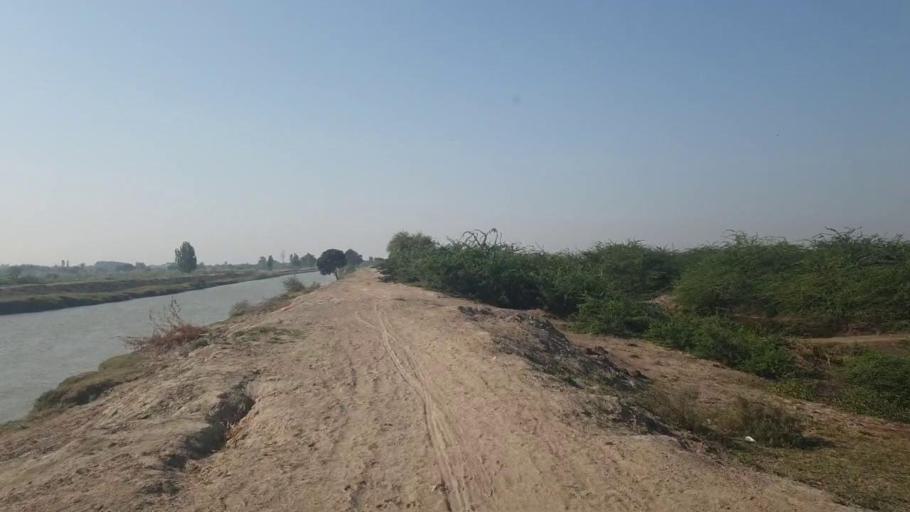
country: PK
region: Sindh
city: Badin
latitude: 24.6924
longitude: 68.8698
